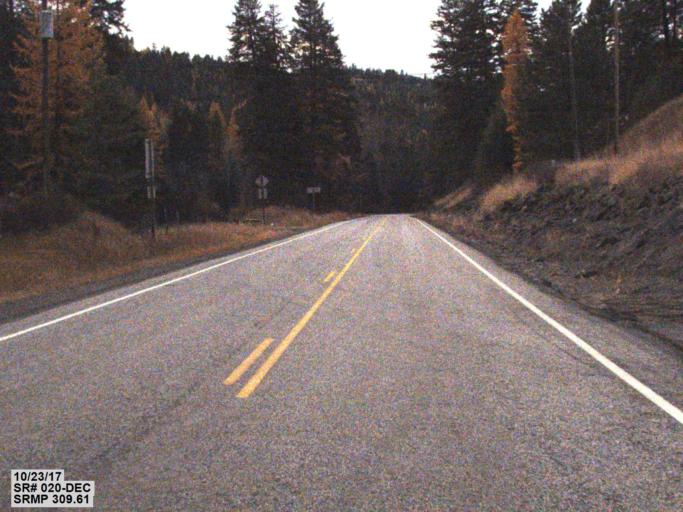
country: US
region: Washington
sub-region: Ferry County
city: Republic
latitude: 48.5973
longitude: -118.6441
